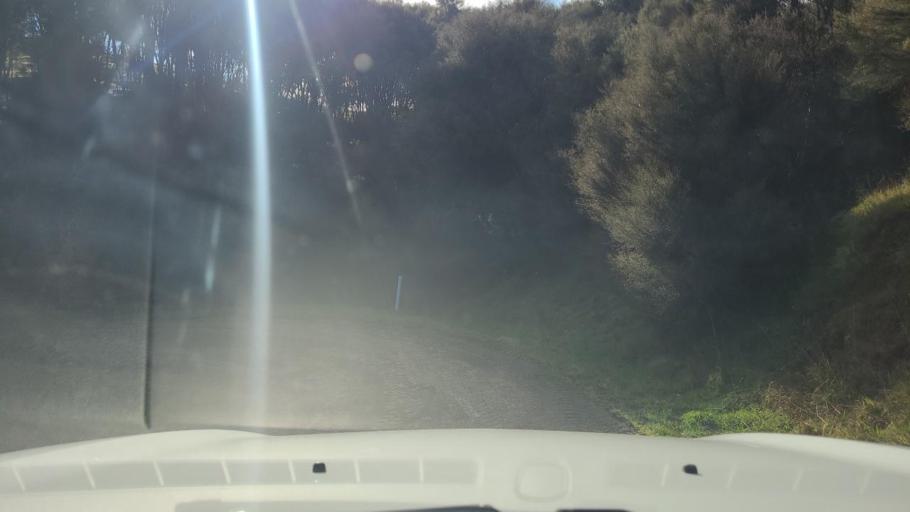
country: NZ
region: Wellington
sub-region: South Wairarapa District
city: Waipawa
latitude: -41.2402
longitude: 175.7009
